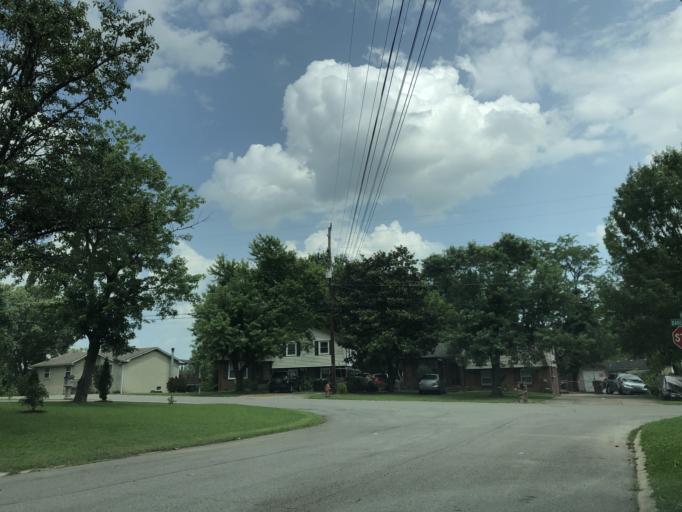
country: US
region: Tennessee
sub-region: Williamson County
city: Brentwood Estates
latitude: 36.0574
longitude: -86.6830
